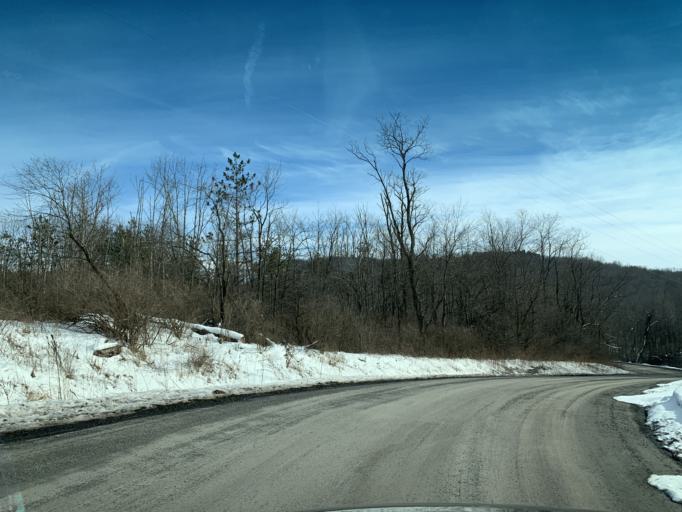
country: US
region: Maryland
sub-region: Allegany County
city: Frostburg
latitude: 39.6198
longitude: -78.9324
